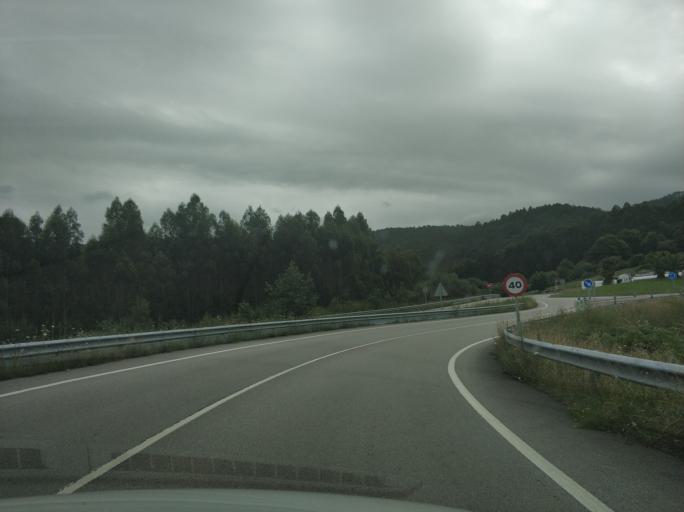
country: ES
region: Asturias
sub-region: Province of Asturias
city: Cudillero
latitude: 43.5647
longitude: -6.2416
